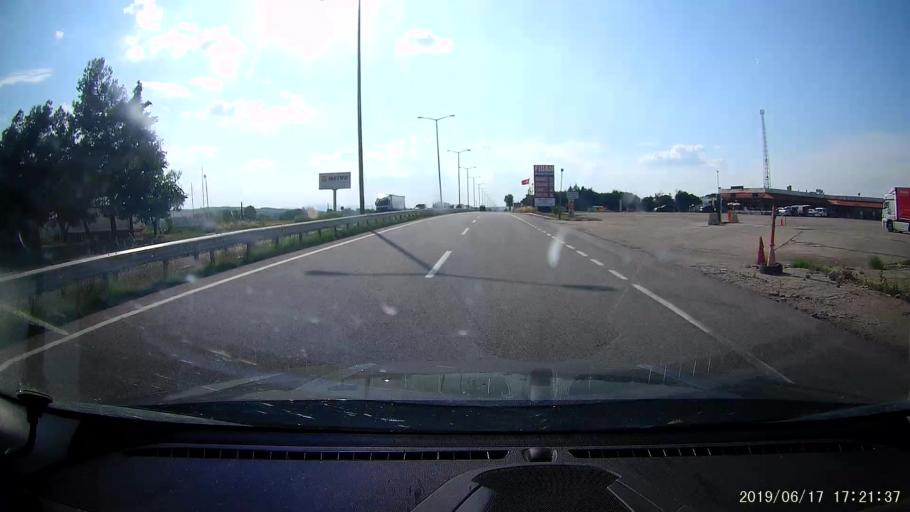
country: GR
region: East Macedonia and Thrace
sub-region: Nomos Evrou
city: Rizia
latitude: 41.7069
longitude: 26.3911
